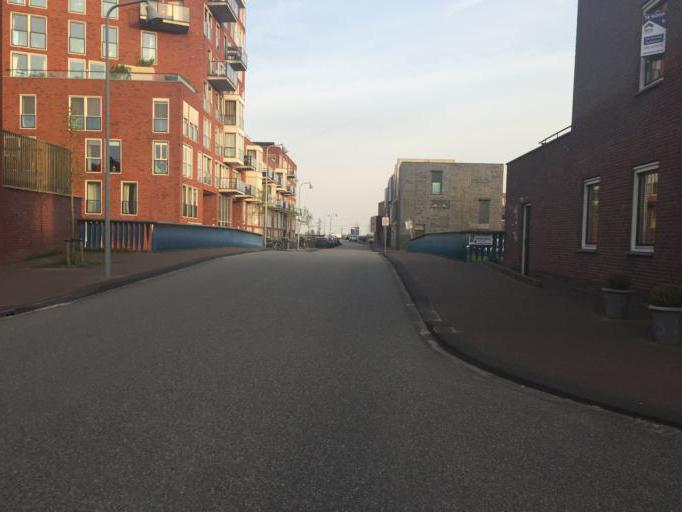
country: NL
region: Utrecht
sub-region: Gemeente Woerden
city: Woerden
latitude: 52.0874
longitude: 4.9163
